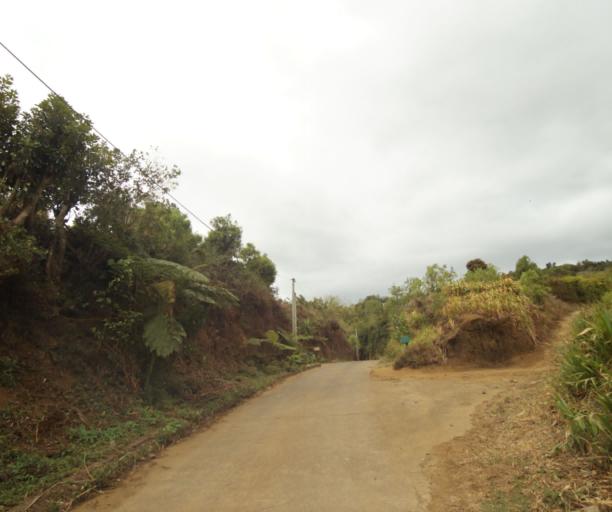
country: RE
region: Reunion
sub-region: Reunion
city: Saint-Paul
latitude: -21.0168
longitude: 55.3299
